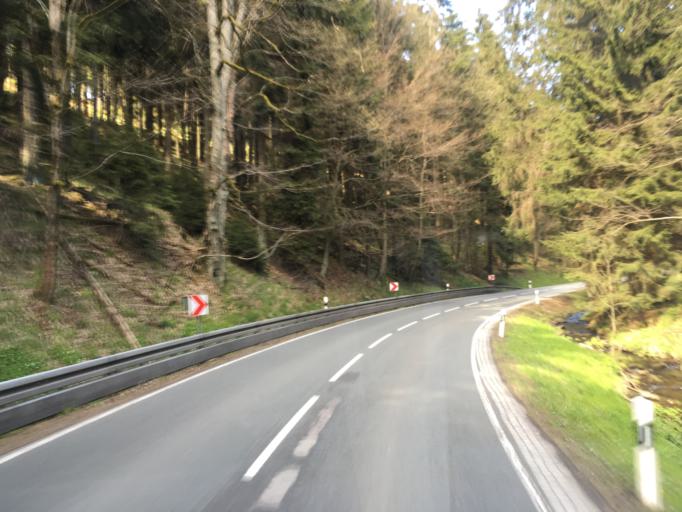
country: DE
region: Saxony-Anhalt
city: Hasselfelde
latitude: 51.6411
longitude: 10.8133
